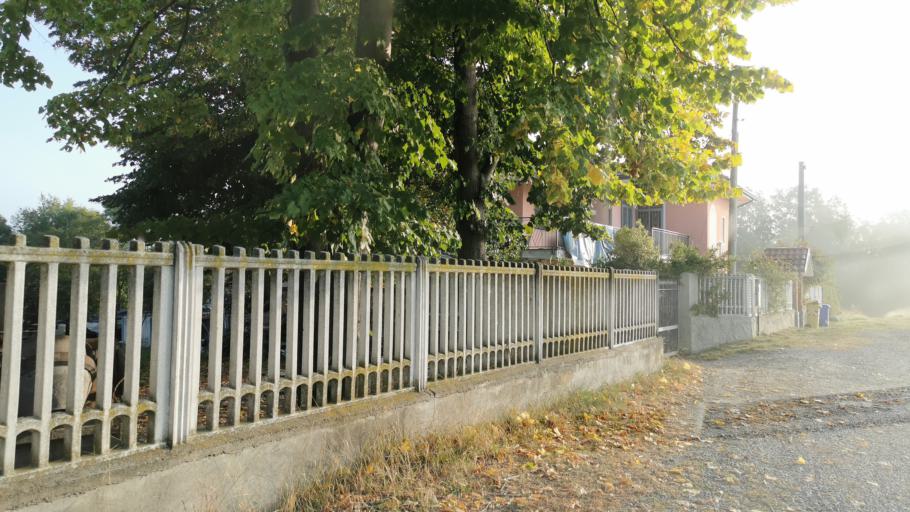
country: IT
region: Piedmont
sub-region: Provincia di Torino
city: Front
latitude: 45.2592
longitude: 7.6623
